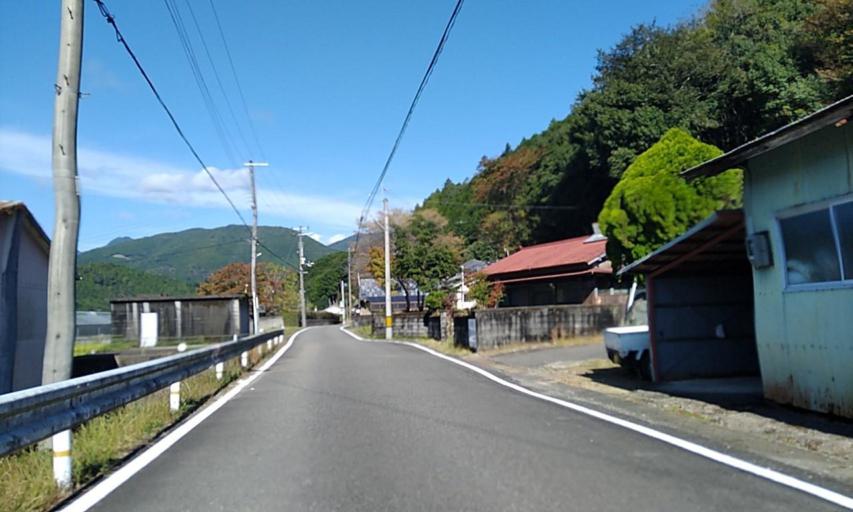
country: JP
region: Wakayama
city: Shingu
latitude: 33.9248
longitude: 135.9836
